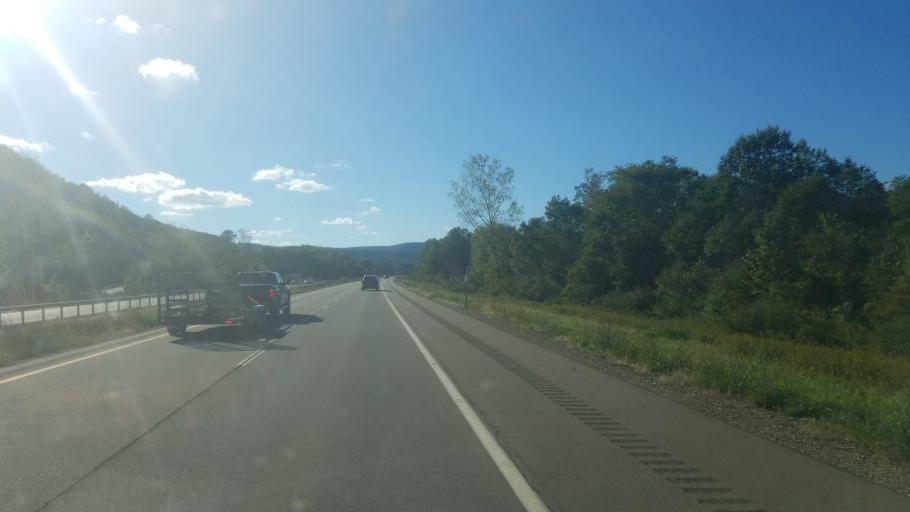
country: US
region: Pennsylvania
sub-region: McKean County
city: Foster Brook
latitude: 42.0858
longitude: -78.6088
